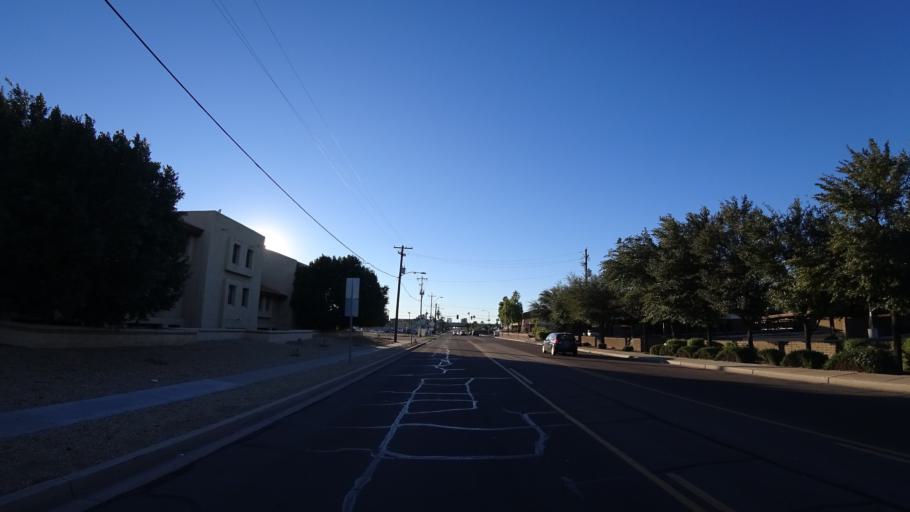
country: US
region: Arizona
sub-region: Maricopa County
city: Phoenix
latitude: 33.4875
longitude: -112.0377
